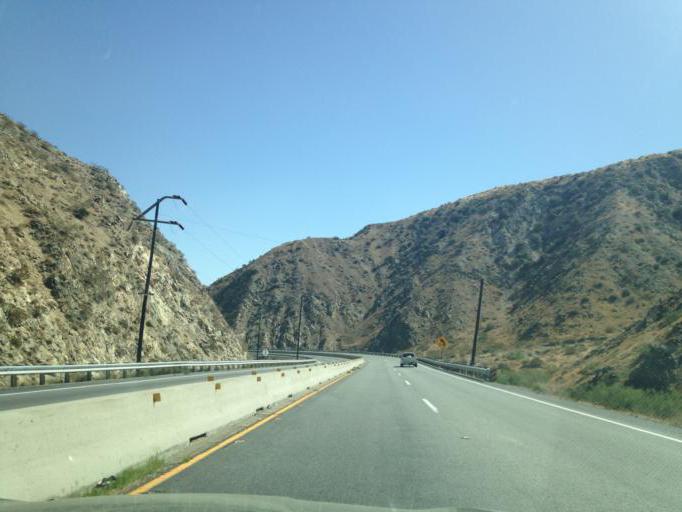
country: US
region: California
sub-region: San Bernardino County
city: Morongo Valley
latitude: 34.0317
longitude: -116.5911
